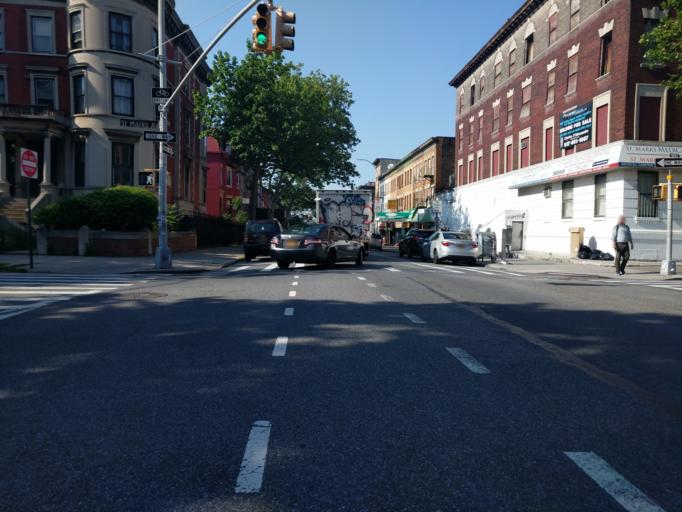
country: US
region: New York
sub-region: Kings County
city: Brooklyn
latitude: 40.6746
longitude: -73.9418
